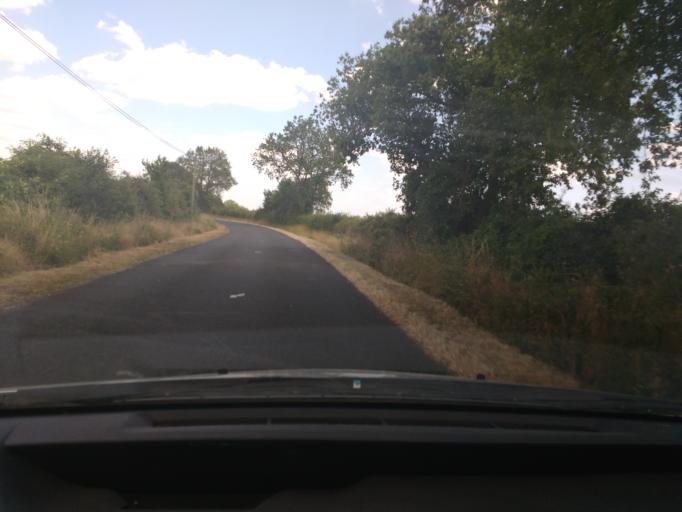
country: FR
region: Pays de la Loire
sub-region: Departement de Maine-et-Loire
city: Bauge-en-Anjou
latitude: 47.5473
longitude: -0.0549
